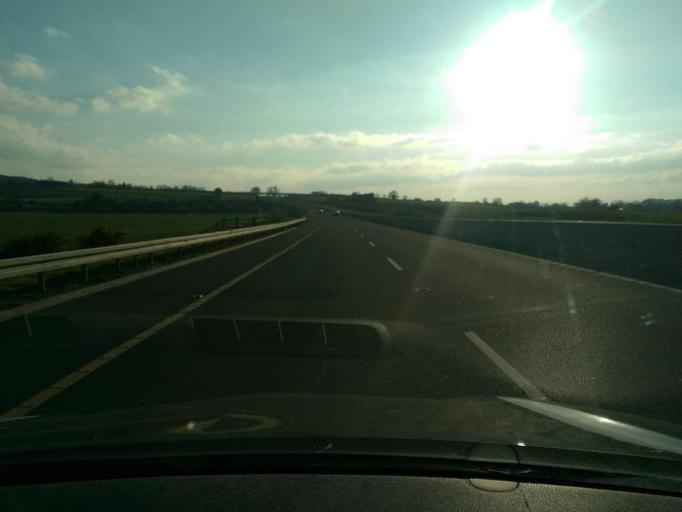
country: IE
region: Munster
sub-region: North Tipperary
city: Roscrea
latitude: 52.9053
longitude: -7.8919
